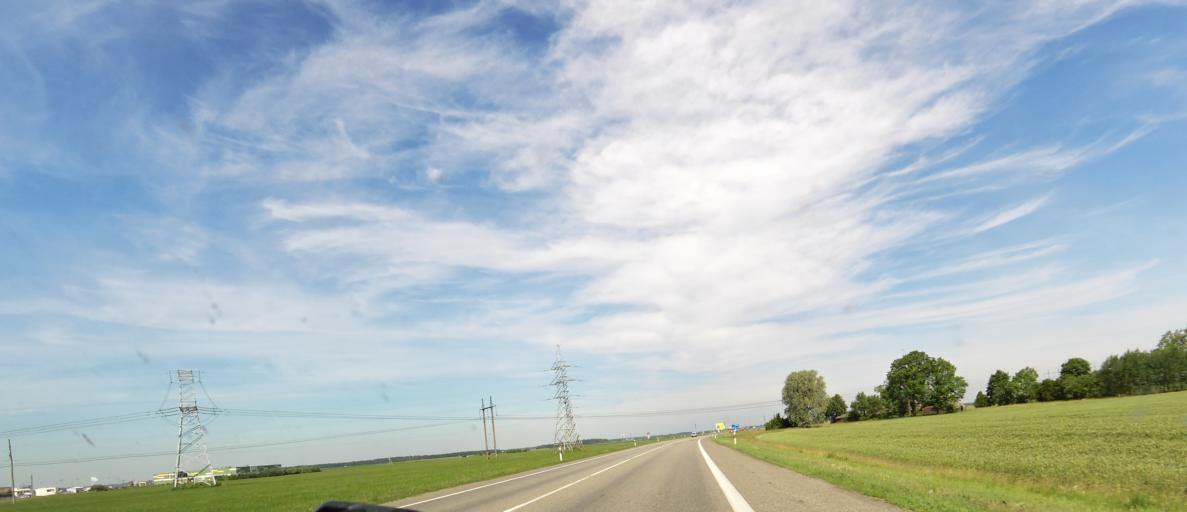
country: LT
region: Panevezys
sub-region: Panevezys City
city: Panevezys
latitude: 55.6856
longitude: 24.2856
